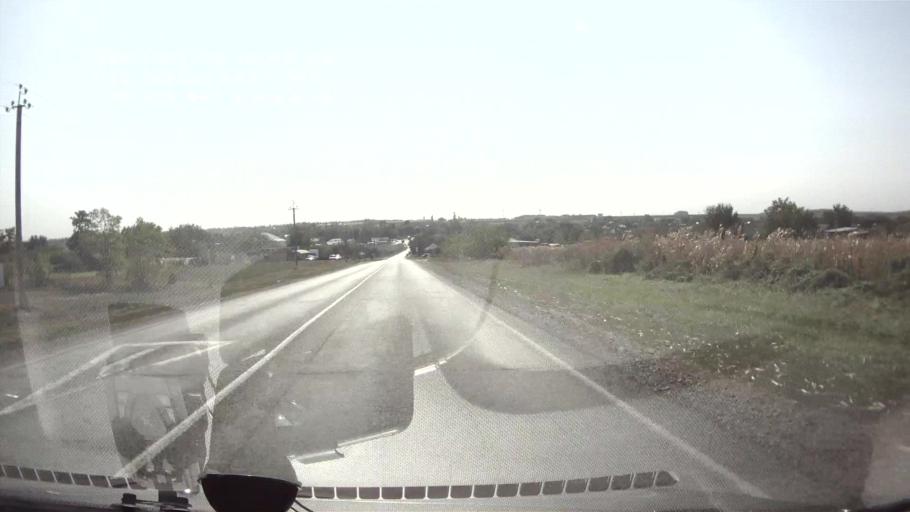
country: RU
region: Krasnodarskiy
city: Dmitriyevskaya
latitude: 45.6584
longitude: 40.7520
